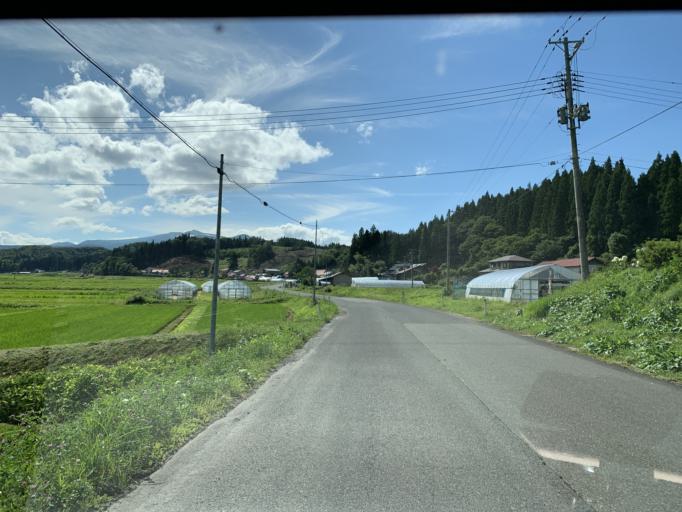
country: JP
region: Iwate
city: Ichinoseki
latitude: 38.9635
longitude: 140.9540
